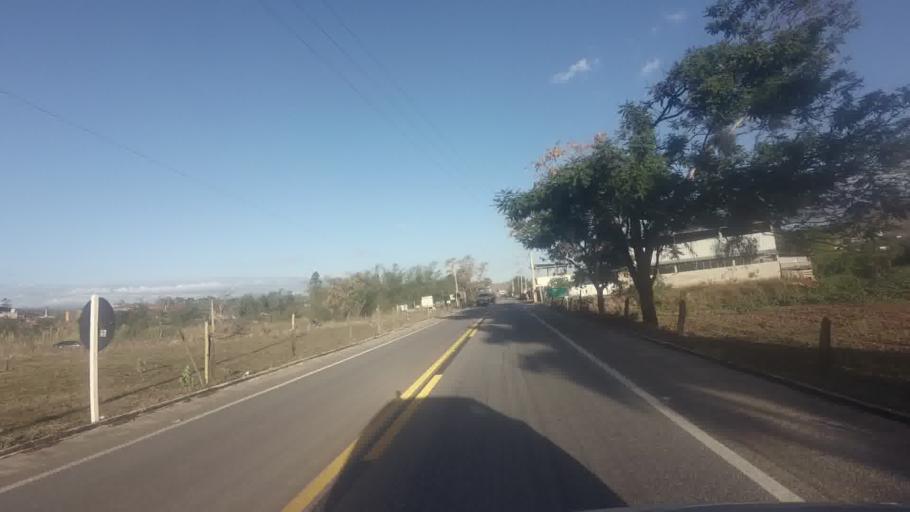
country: BR
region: Espirito Santo
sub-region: Cachoeiro De Itapemirim
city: Cachoeiro de Itapemirim
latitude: -20.8263
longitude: -41.1858
